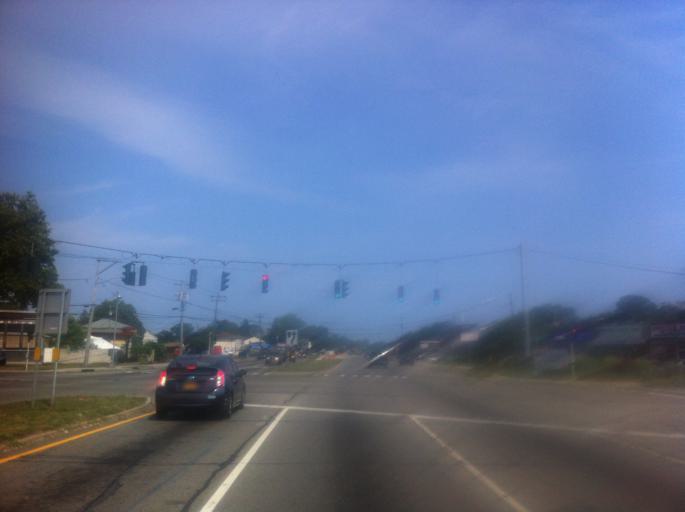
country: US
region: New York
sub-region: Suffolk County
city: North Lindenhurst
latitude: 40.7145
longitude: -73.3847
